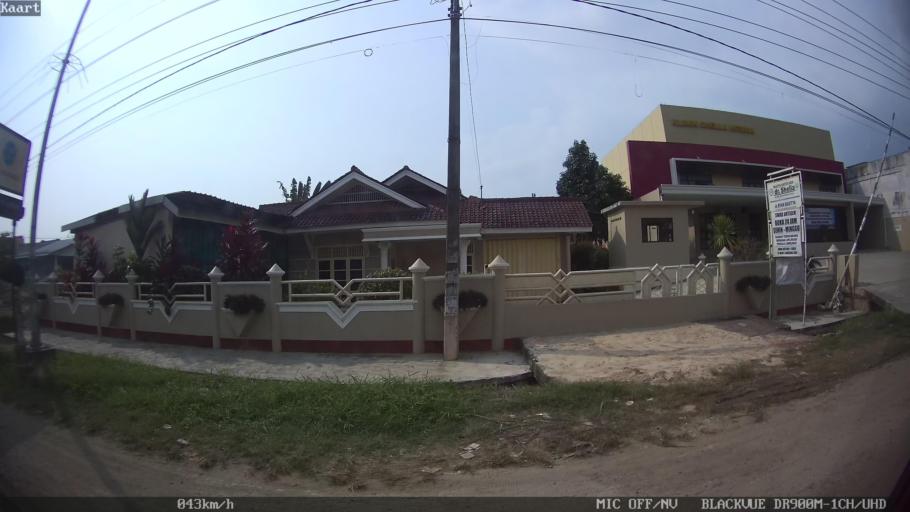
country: ID
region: Lampung
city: Gadingrejo
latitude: -5.3824
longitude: 105.0209
